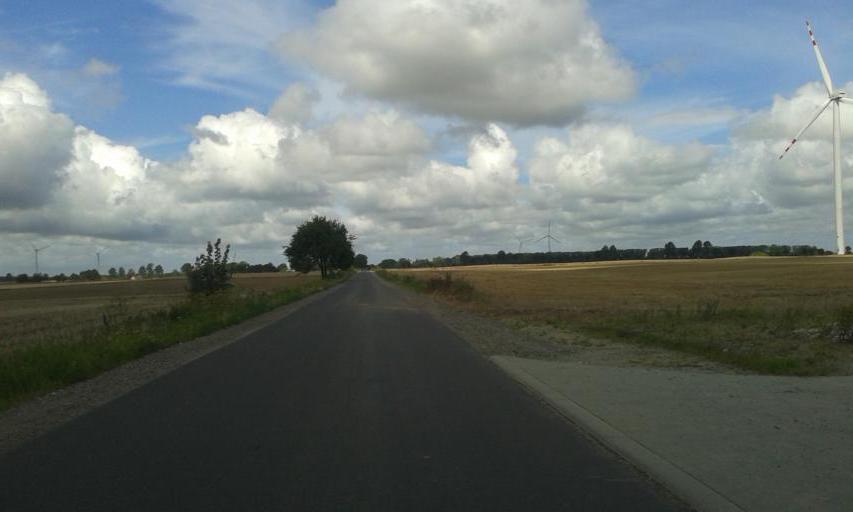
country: PL
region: West Pomeranian Voivodeship
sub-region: Powiat slawienski
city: Slawno
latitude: 54.3224
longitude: 16.5860
